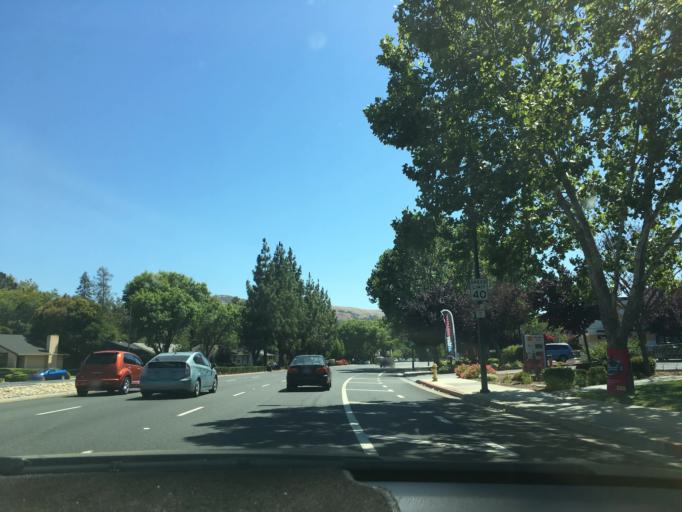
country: US
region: California
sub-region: Santa Clara County
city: Seven Trees
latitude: 37.2323
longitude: -121.7725
